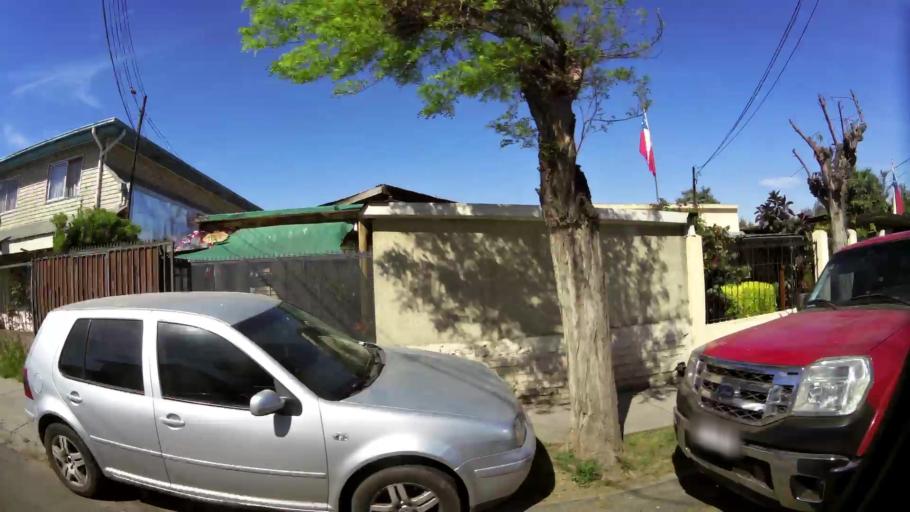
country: CL
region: Santiago Metropolitan
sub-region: Provincia de Santiago
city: Lo Prado
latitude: -33.4986
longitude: -70.7188
